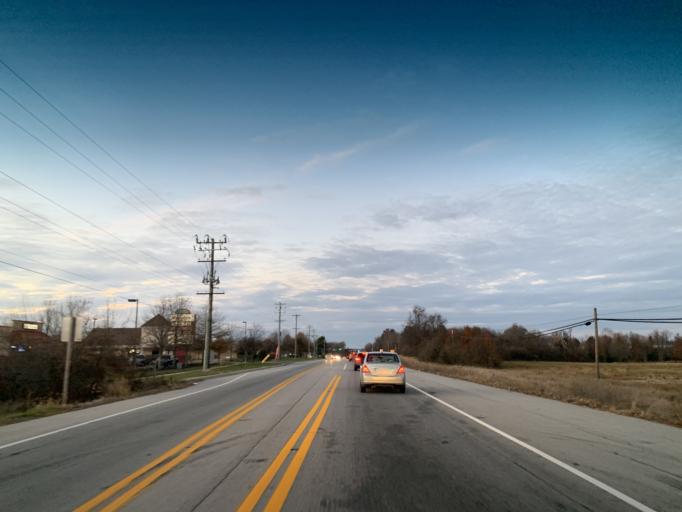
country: US
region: Maryland
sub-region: Cecil County
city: Elkton
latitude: 39.5883
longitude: -75.8236
